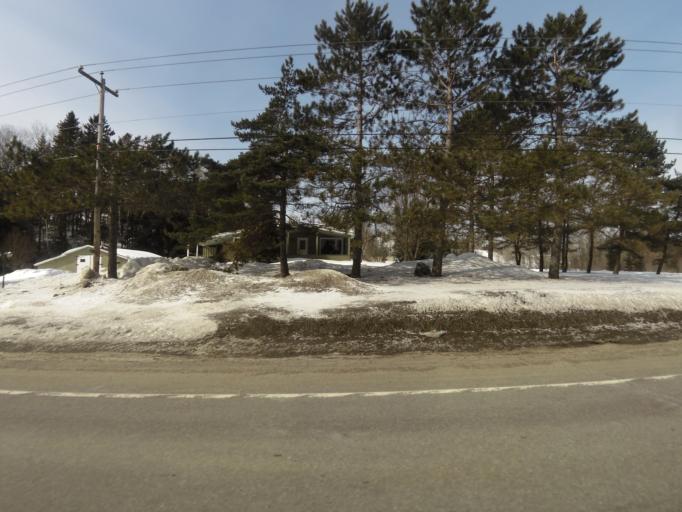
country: CA
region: Quebec
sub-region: Laurentides
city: Mont-Laurier
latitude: 46.5785
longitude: -75.4782
